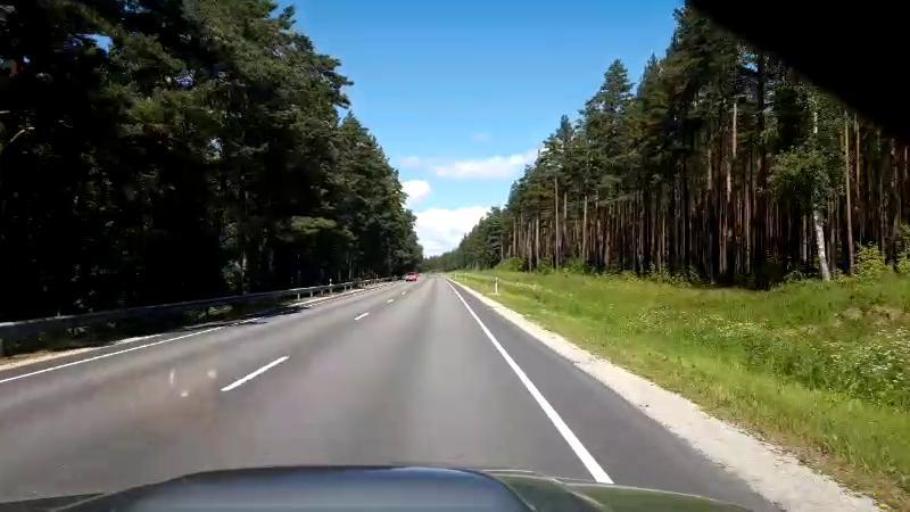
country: EE
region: Paernumaa
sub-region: Paernu linn
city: Parnu
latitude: 58.1607
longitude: 24.4980
